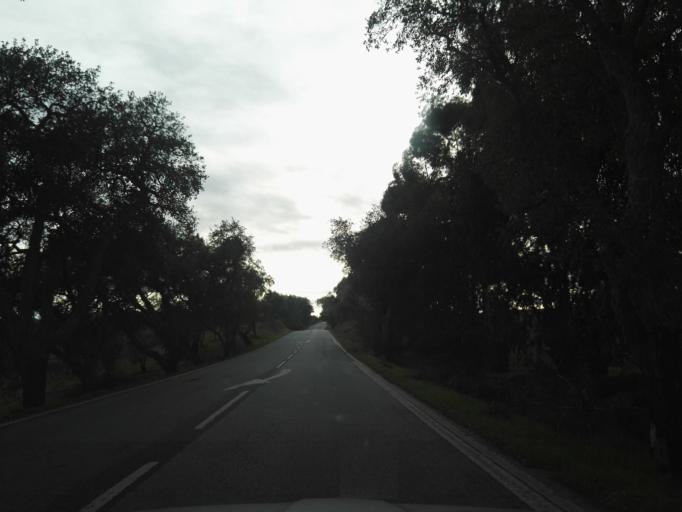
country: PT
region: Evora
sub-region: Redondo
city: Redondo
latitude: 38.6598
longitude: -7.5304
